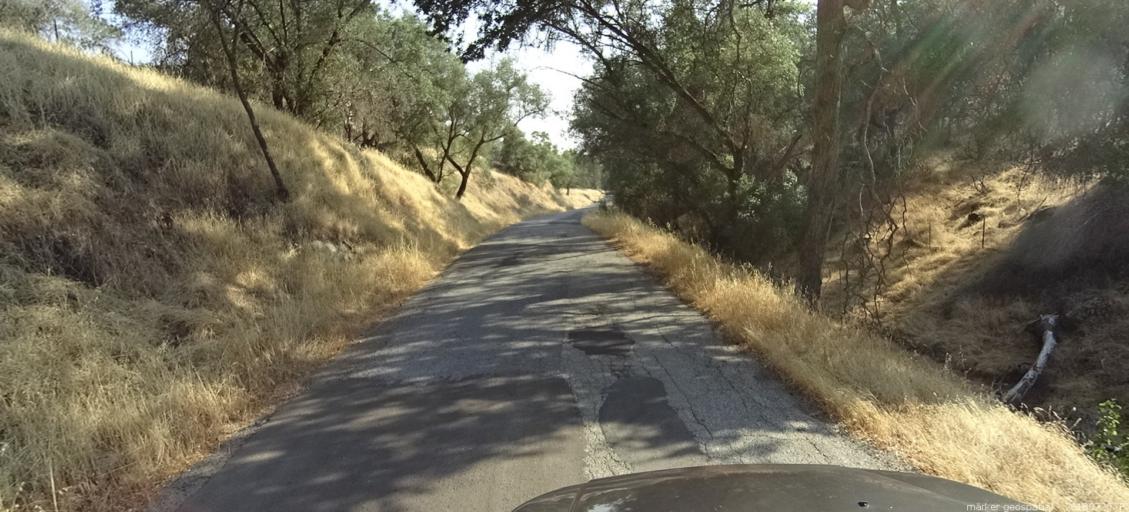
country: US
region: California
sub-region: Madera County
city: Yosemite Lakes
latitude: 37.2393
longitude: -119.9052
